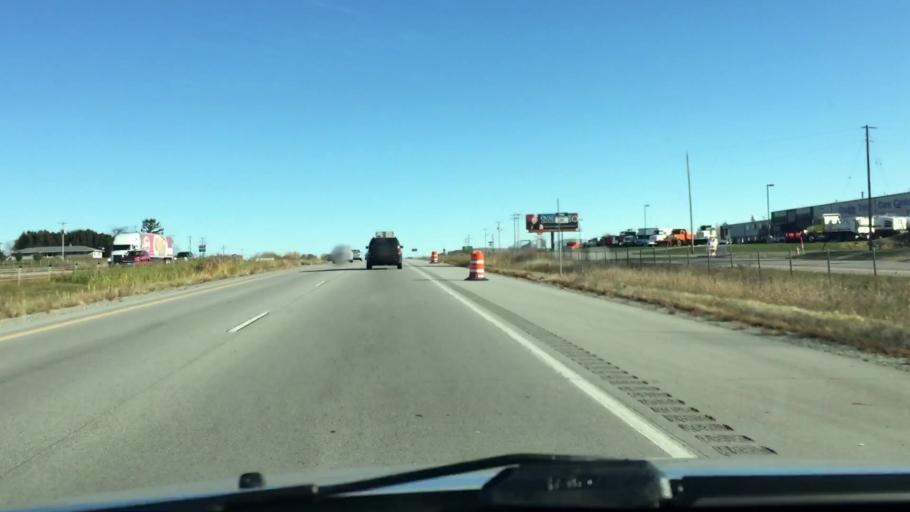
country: US
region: Wisconsin
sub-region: Brown County
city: De Pere
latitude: 44.4140
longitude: -88.1351
